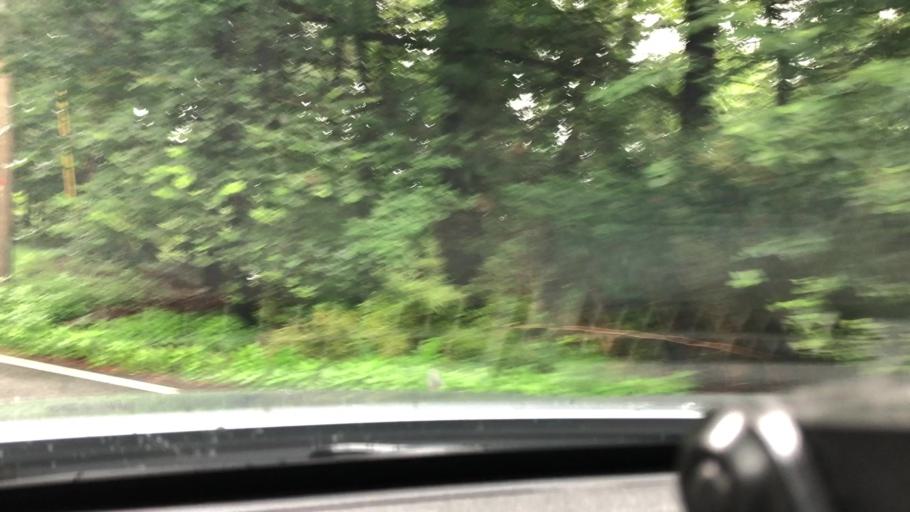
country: US
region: New Jersey
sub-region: Bergen County
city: Woodcliff Lake
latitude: 41.0355
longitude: -74.0820
